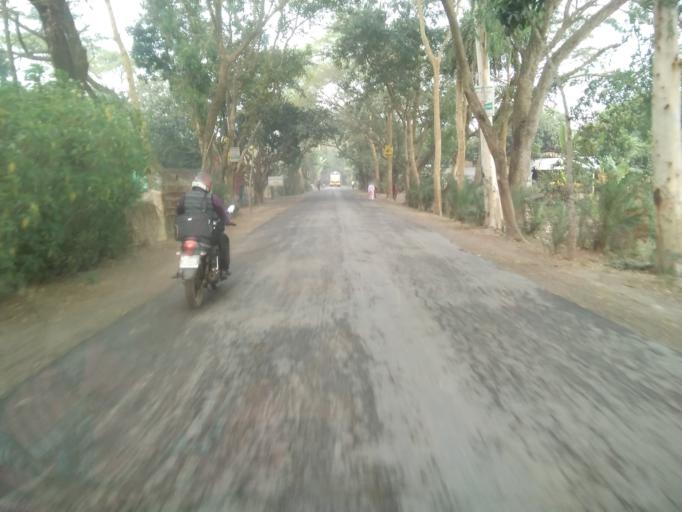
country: BD
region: Khulna
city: Satkhira
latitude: 22.6760
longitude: 89.0168
